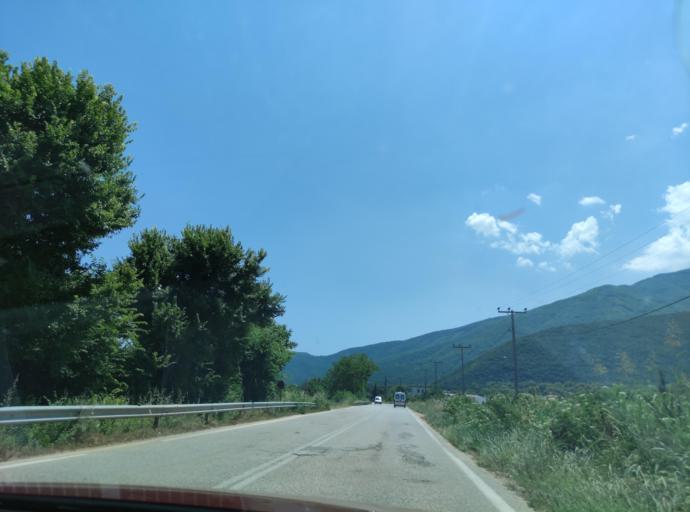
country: GR
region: East Macedonia and Thrace
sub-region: Nomos Kavalas
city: Palaiochori
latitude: 40.9606
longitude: 24.1876
